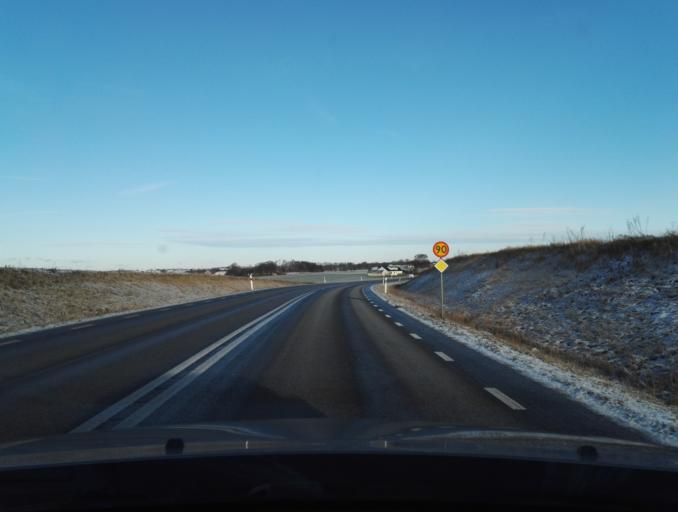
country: SE
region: Skane
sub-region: Trelleborgs Kommun
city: Trelleborg
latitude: 55.4226
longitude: 13.1748
